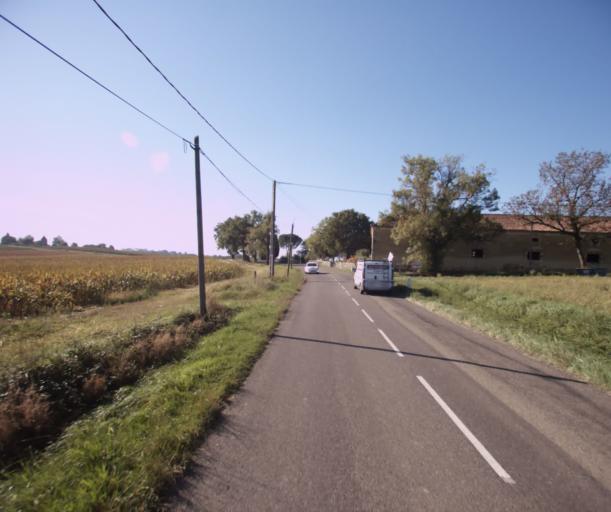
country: FR
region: Aquitaine
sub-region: Departement des Landes
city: Gabarret
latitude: 43.9211
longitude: 0.0170
